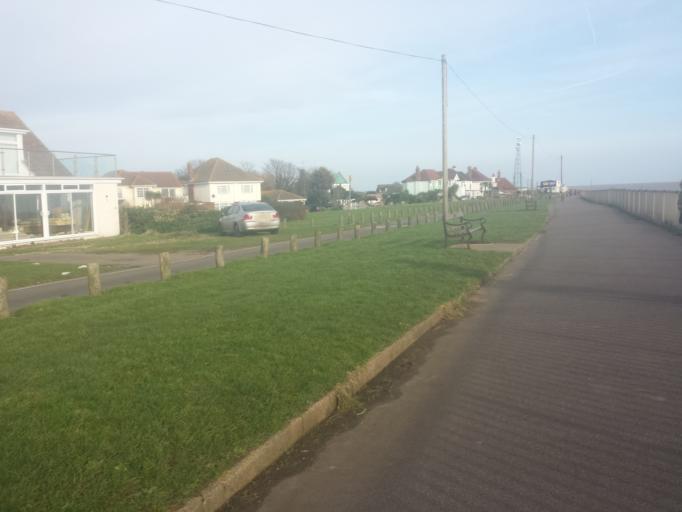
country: GB
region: England
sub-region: Essex
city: Frinton-on-Sea
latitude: 51.8049
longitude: 1.2061
